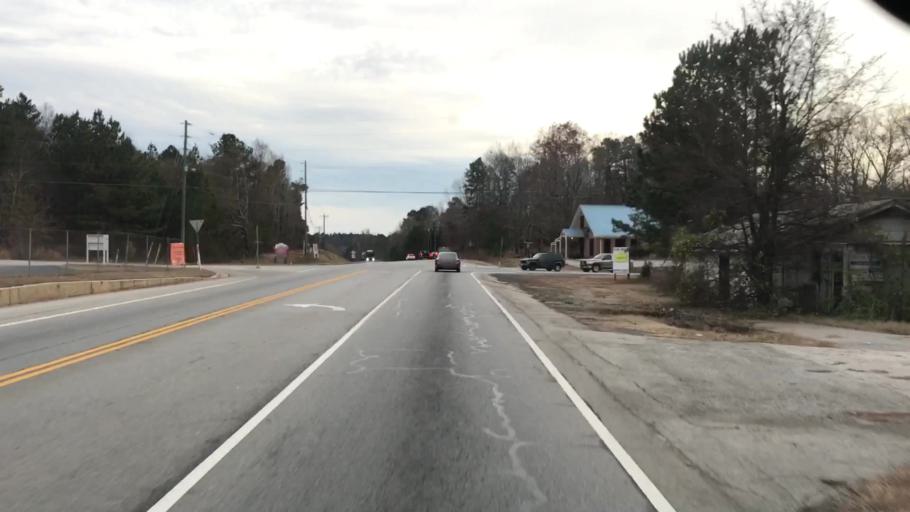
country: US
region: Georgia
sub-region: Jackson County
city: Hoschton
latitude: 34.0443
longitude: -83.7770
